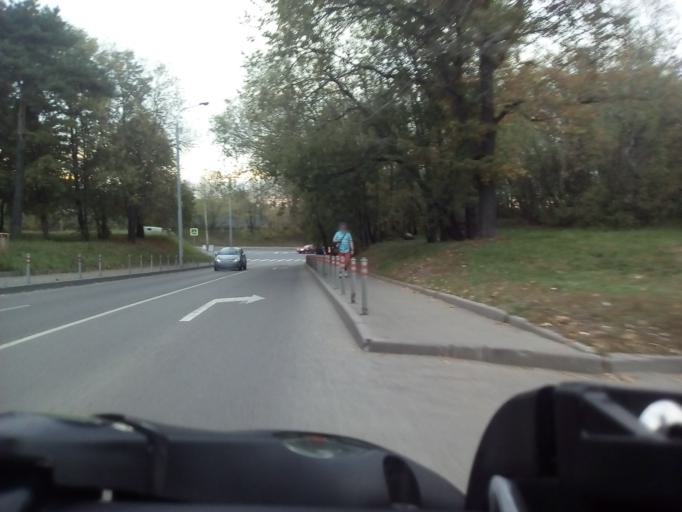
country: RU
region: Moscow
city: Sviblovo
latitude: 55.8450
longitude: 37.6376
